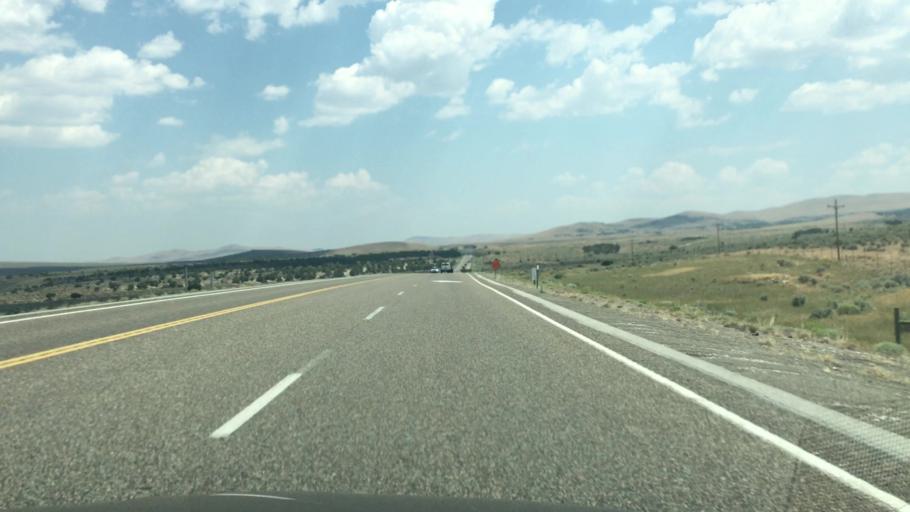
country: US
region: Nevada
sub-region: Elko County
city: Wells
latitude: 41.1930
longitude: -114.8684
